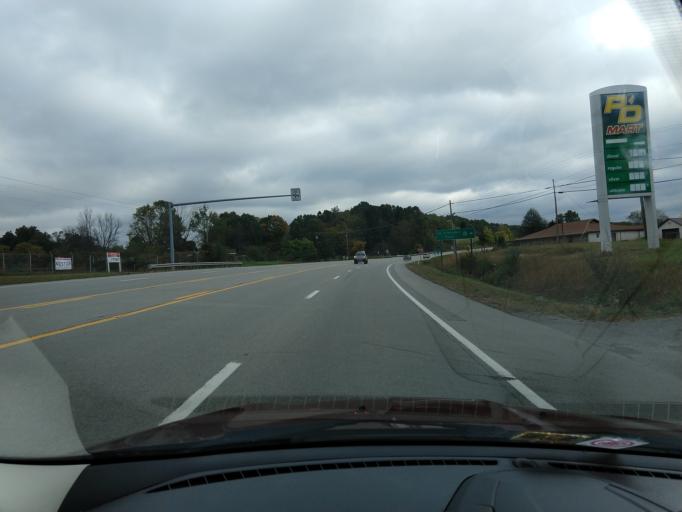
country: US
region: West Virginia
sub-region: Randolph County
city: Elkins
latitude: 38.8623
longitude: -79.8584
